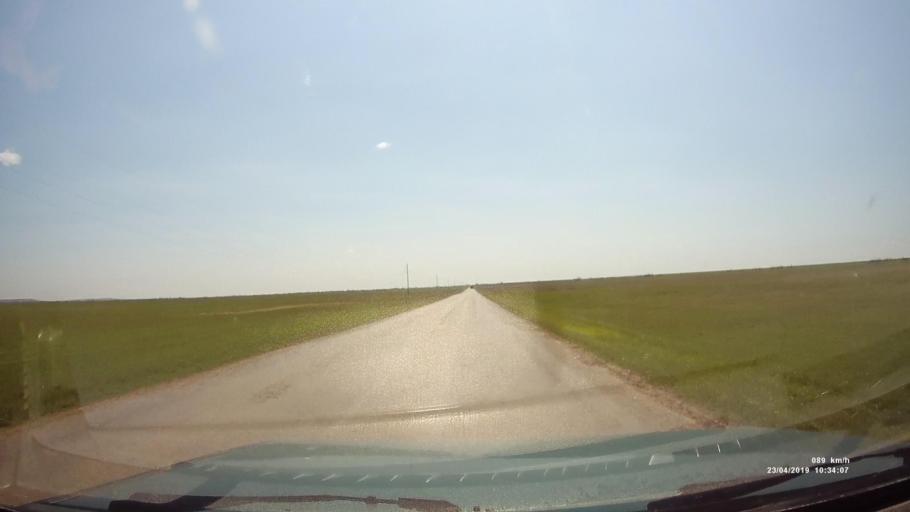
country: RU
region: Kalmykiya
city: Yashalta
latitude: 46.5671
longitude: 42.6061
